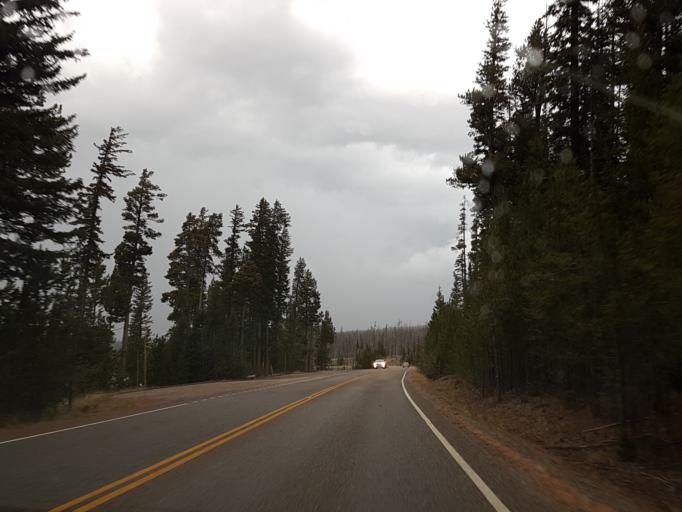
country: US
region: Montana
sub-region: Gallatin County
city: West Yellowstone
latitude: 44.4659
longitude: -110.5164
